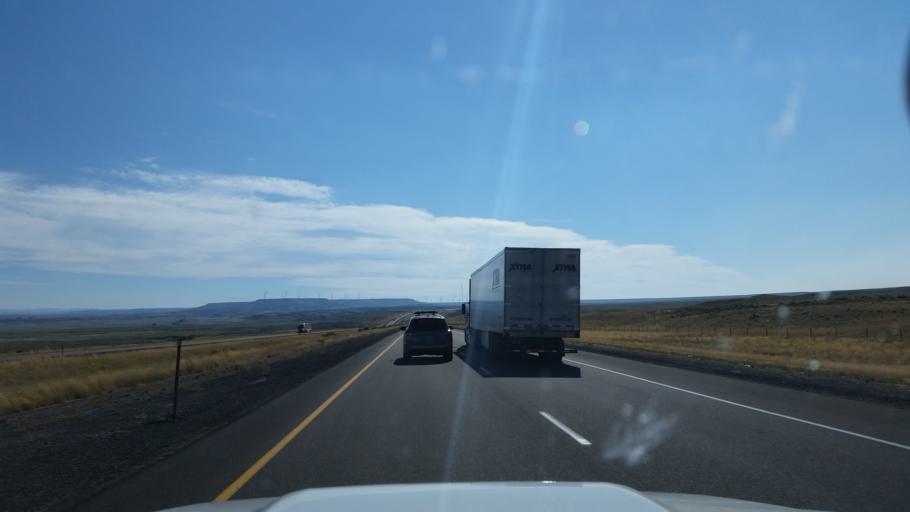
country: US
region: Wyoming
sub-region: Uinta County
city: Mountain View
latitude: 41.3453
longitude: -110.3914
